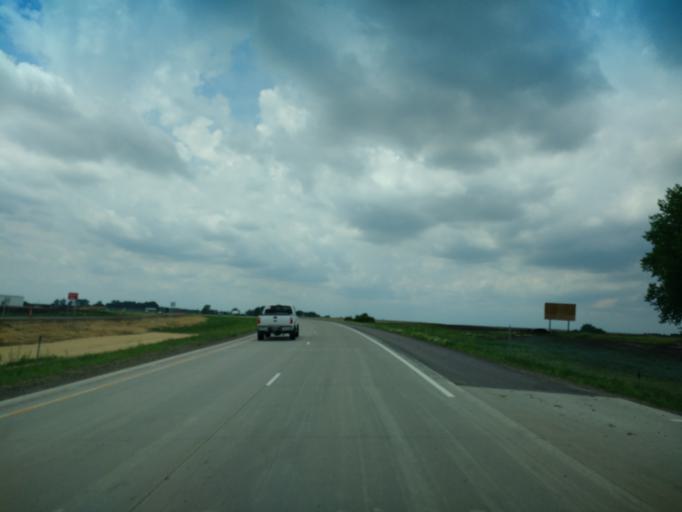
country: US
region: Minnesota
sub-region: Cottonwood County
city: Windom
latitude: 43.9102
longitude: -95.0491
